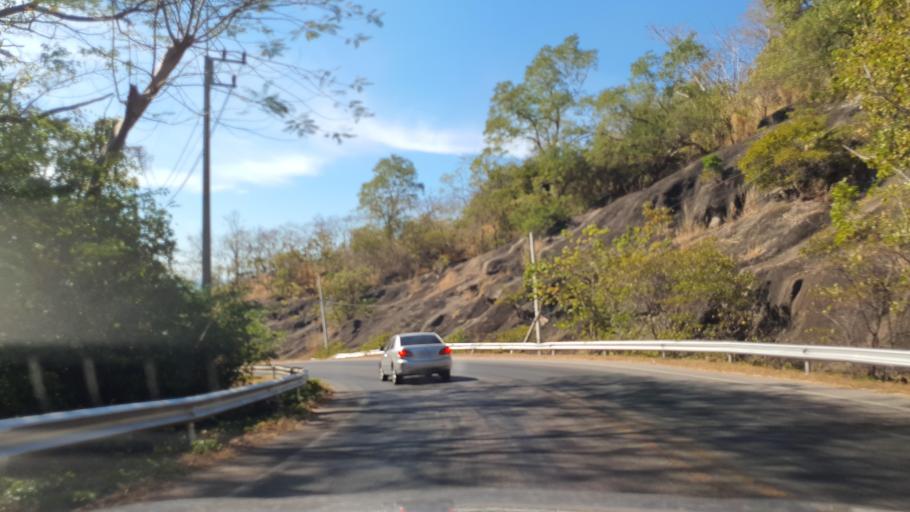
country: TH
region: Kalasin
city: Khao Wong
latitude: 16.7546
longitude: 104.1224
